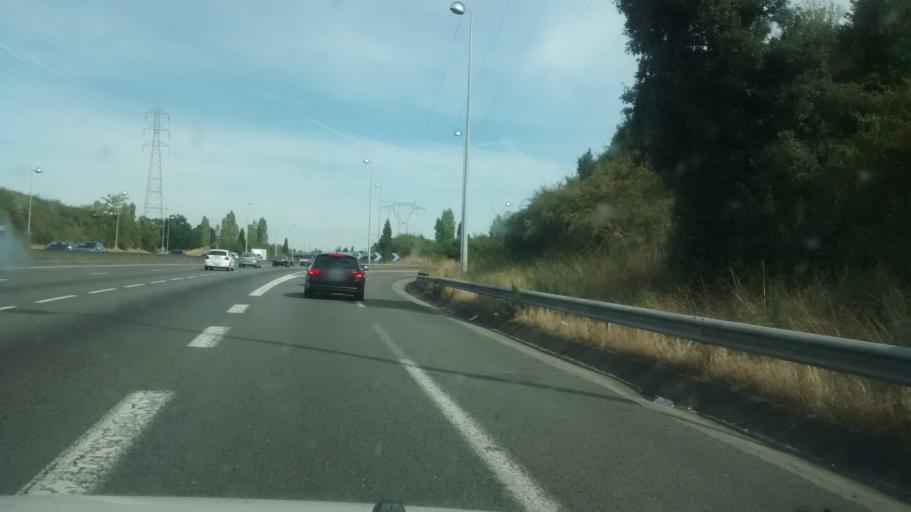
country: FR
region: Aquitaine
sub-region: Departement de la Gironde
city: Floirac
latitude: 44.8398
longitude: -0.5014
